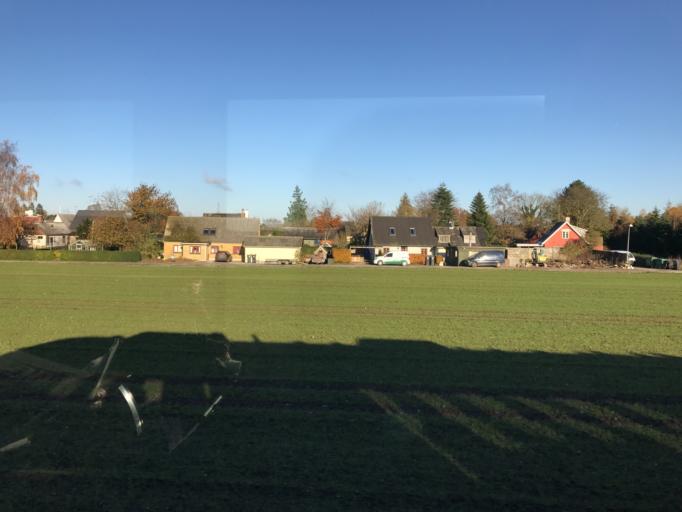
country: DK
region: Zealand
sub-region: Stevns Kommune
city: Store Heddinge
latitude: 55.3183
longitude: 12.3747
